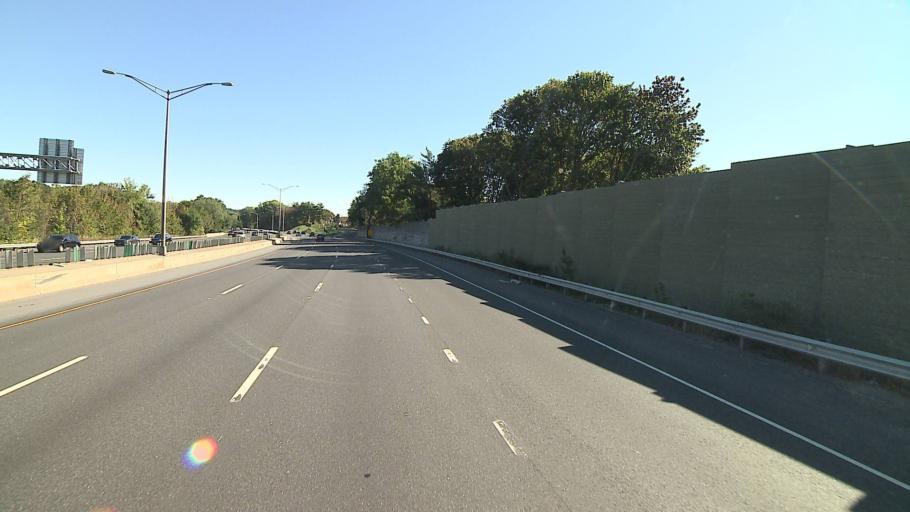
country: US
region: Connecticut
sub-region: Fairfield County
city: Danbury
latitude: 41.4017
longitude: -73.4661
